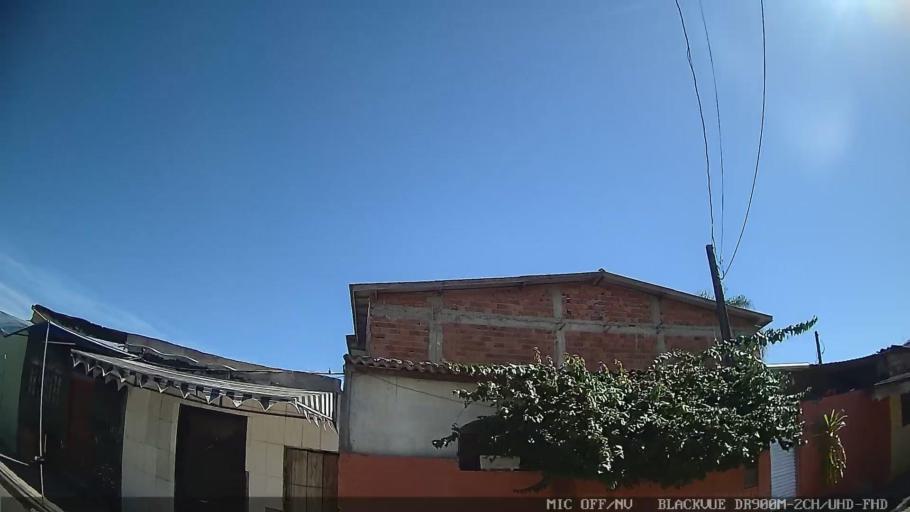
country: BR
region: Sao Paulo
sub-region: Guaruja
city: Guaruja
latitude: -23.9651
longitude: -46.2771
